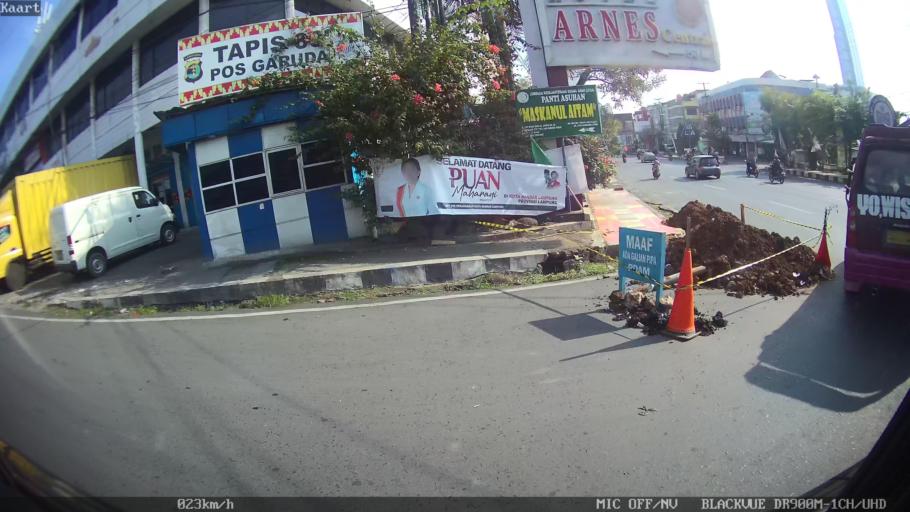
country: ID
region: Lampung
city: Bandarlampung
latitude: -5.4187
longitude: 105.2530
